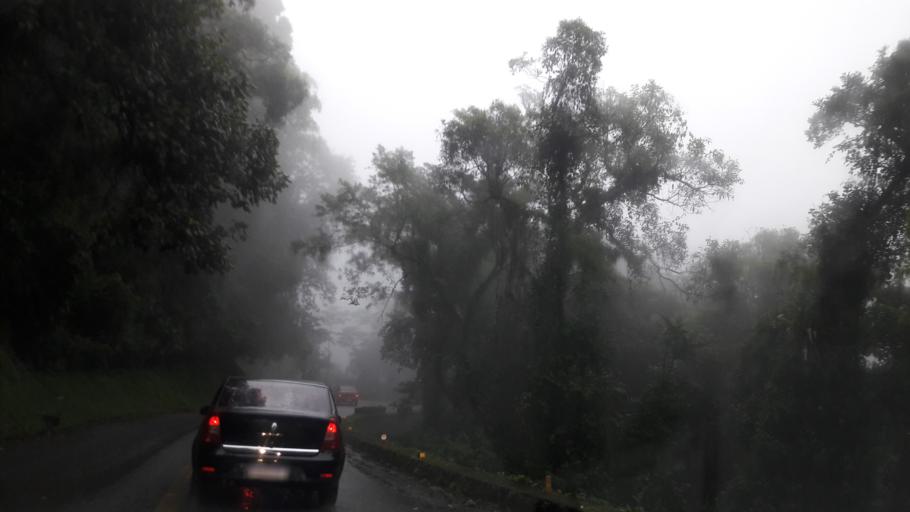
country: BR
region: Parana
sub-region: Campina Grande Do Sul
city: Campina Grande do Sul
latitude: -25.3420
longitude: -48.8916
